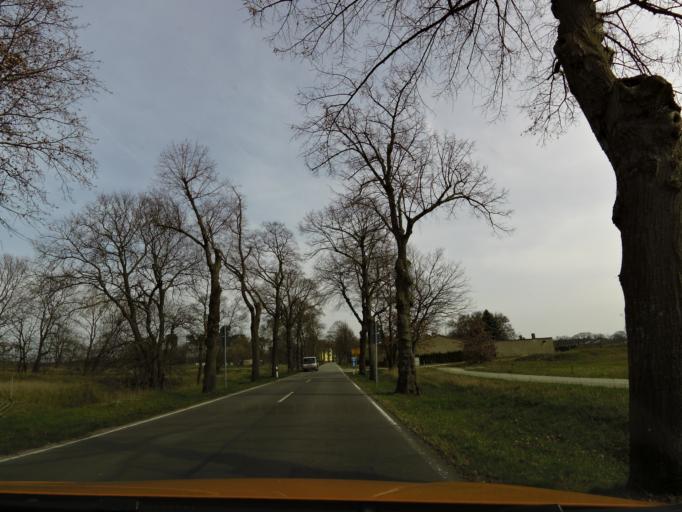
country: DE
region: Brandenburg
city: Stahnsdorf
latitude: 52.3399
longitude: 13.2127
